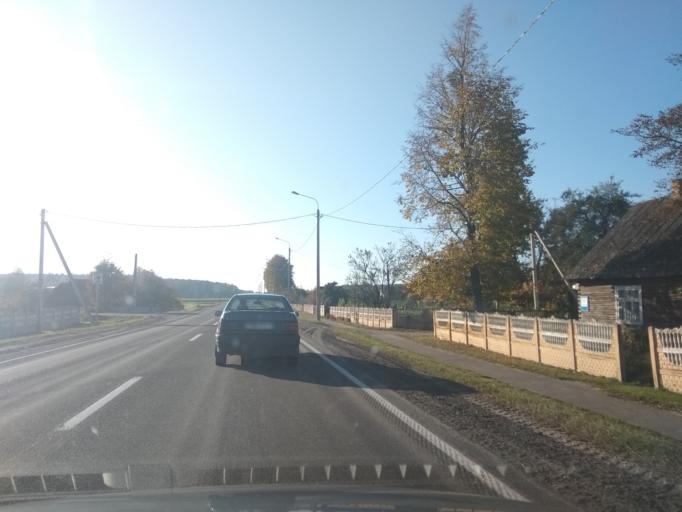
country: BY
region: Grodnenskaya
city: Vyalikaya Byerastavitsa
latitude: 53.1168
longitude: 23.9737
